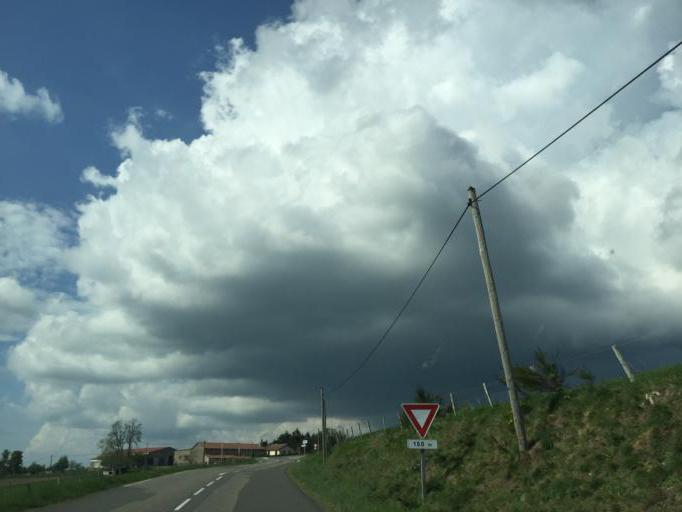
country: FR
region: Rhone-Alpes
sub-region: Departement de la Loire
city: Saint-Genest-Malifaux
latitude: 45.3789
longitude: 4.4903
